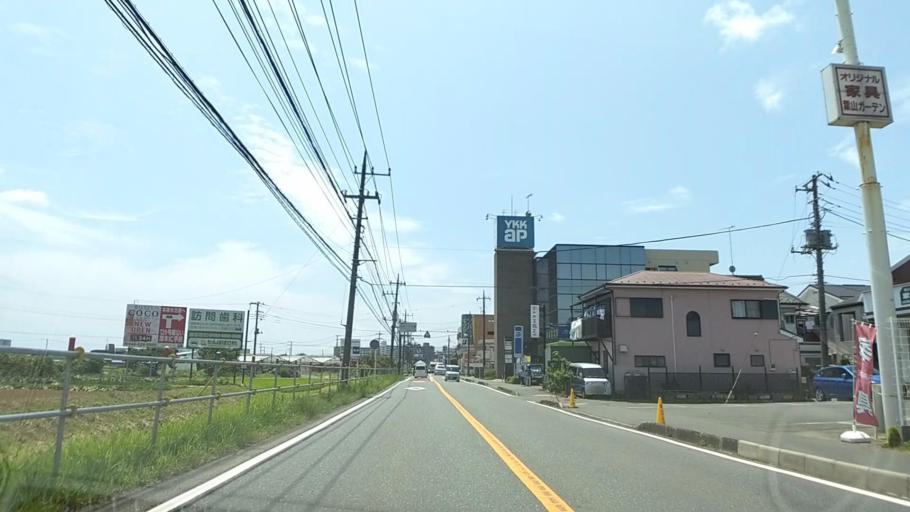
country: JP
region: Kanagawa
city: Atsugi
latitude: 35.4566
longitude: 139.3843
